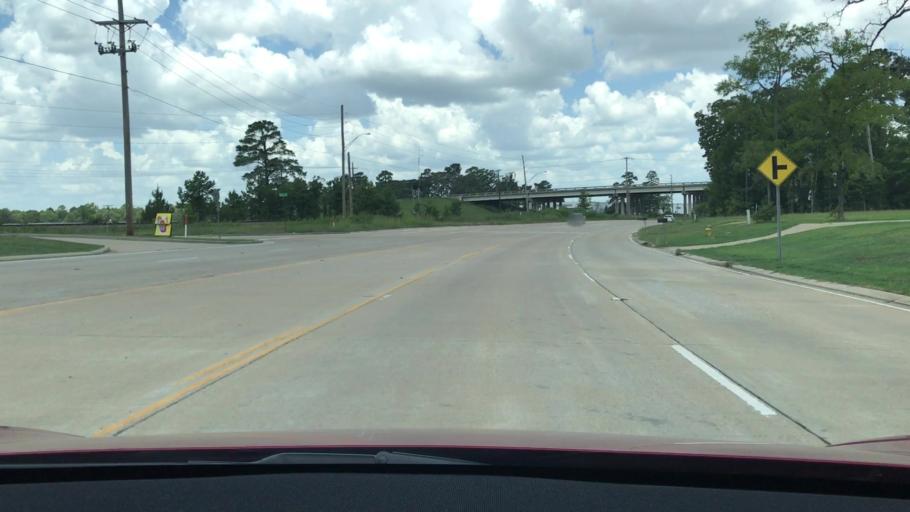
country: US
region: Louisiana
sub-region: Bossier Parish
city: Bossier City
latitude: 32.3991
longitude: -93.7338
